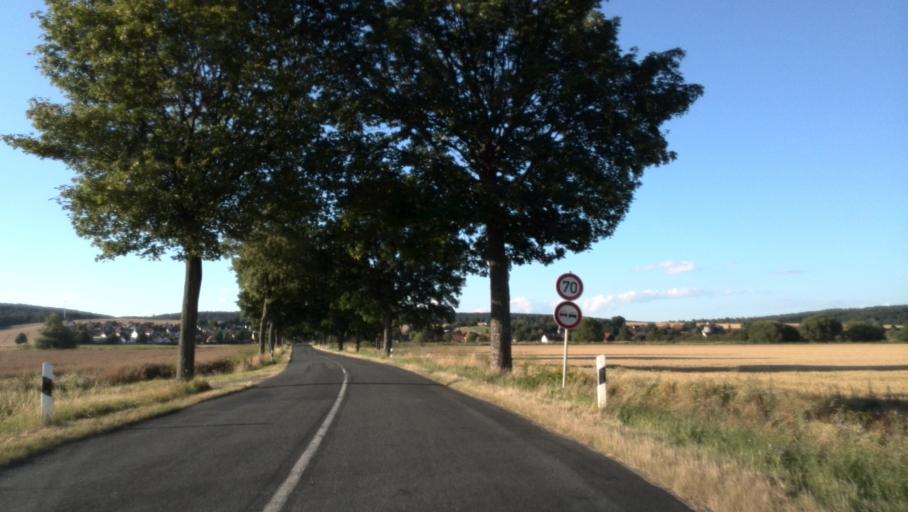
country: DE
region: Lower Saxony
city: Holle
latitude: 52.0985
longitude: 10.1000
